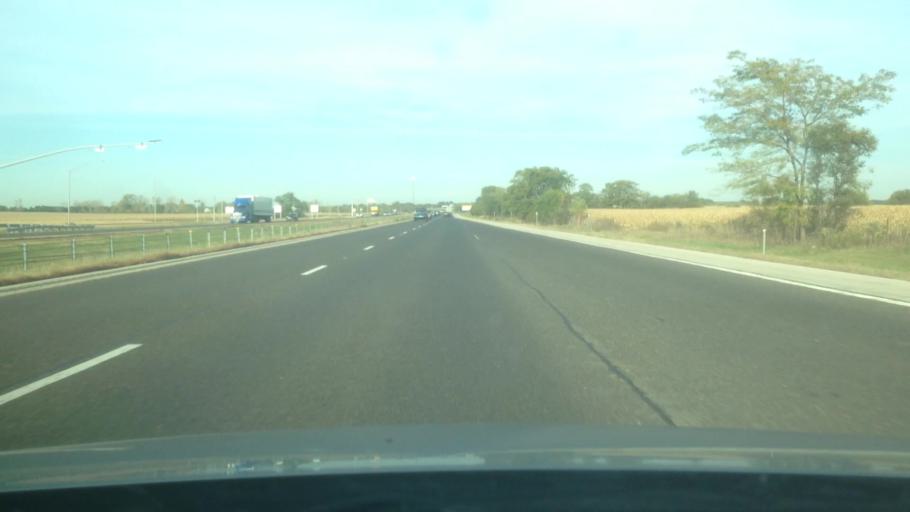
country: US
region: Illinois
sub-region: Will County
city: Peotone
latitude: 41.3658
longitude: -87.7989
